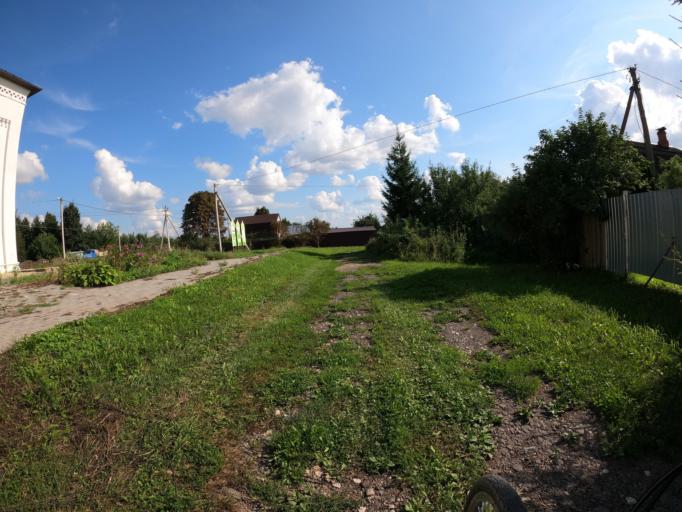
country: RU
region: Moskovskaya
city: Troitskoye
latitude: 55.2133
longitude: 38.4875
